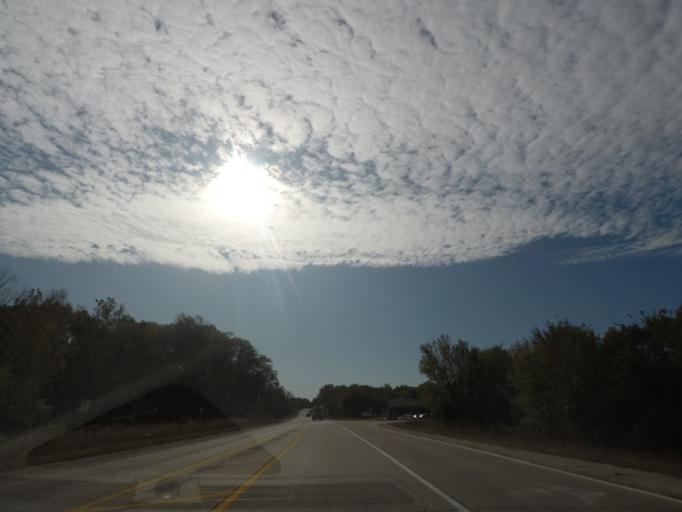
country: US
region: Iowa
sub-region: Story County
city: Ames
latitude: 42.0643
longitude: -93.6229
